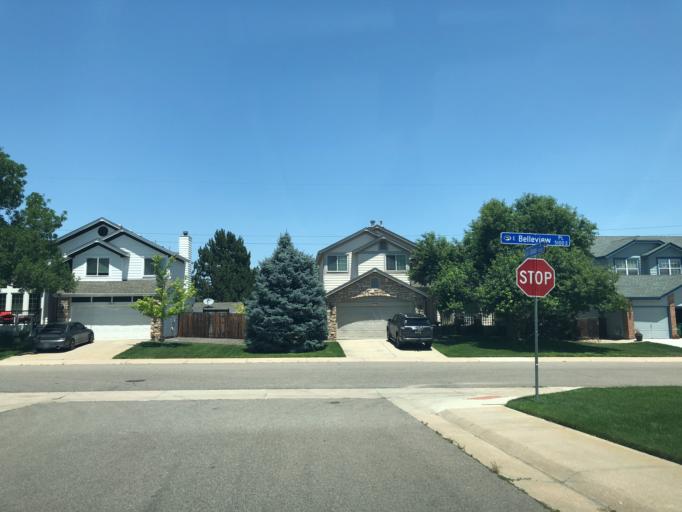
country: US
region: Colorado
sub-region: Arapahoe County
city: Dove Valley
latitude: 39.6234
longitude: -104.7577
